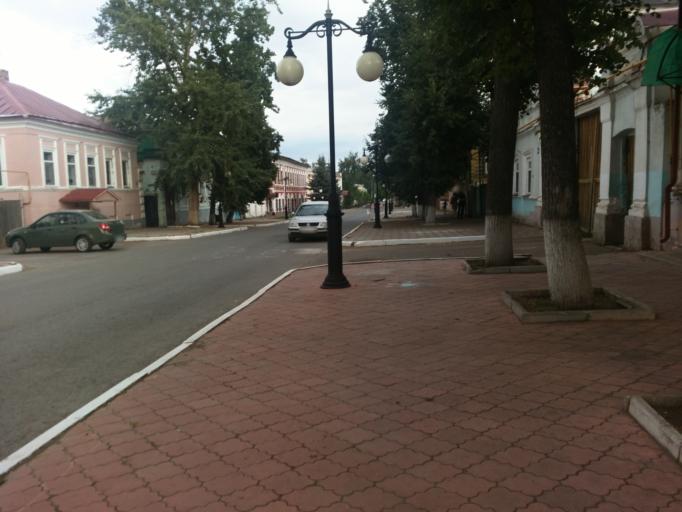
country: RU
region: Tatarstan
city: Yelabuga
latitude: 55.7558
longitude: 52.0600
